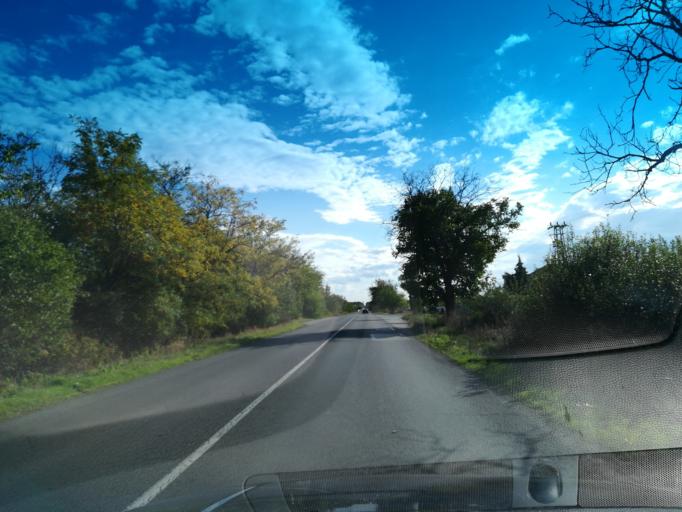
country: BG
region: Stara Zagora
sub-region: Obshtina Stara Zagora
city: Stara Zagora
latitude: 42.3683
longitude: 25.6538
